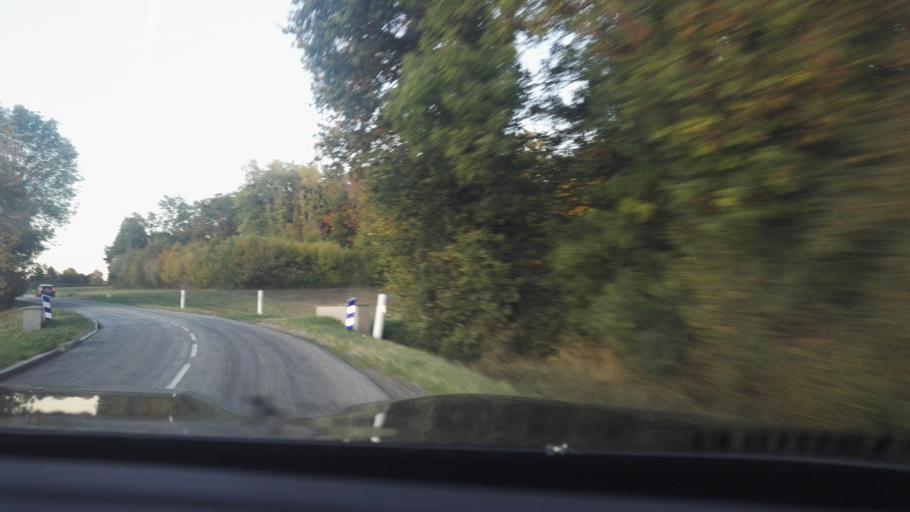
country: FR
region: Ile-de-France
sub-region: Departement des Yvelines
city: Longnes
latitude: 48.8956
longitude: 1.5829
